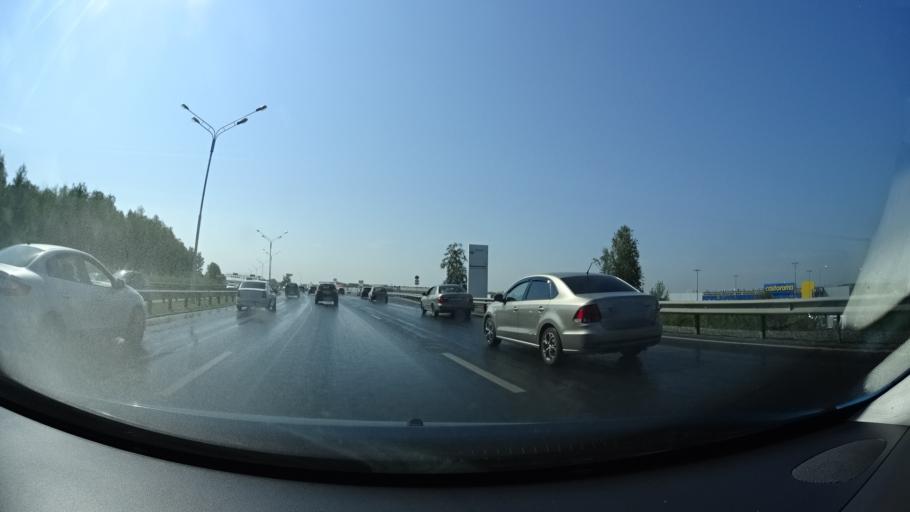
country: RU
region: Bashkortostan
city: Ufa
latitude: 54.6814
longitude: 55.9339
